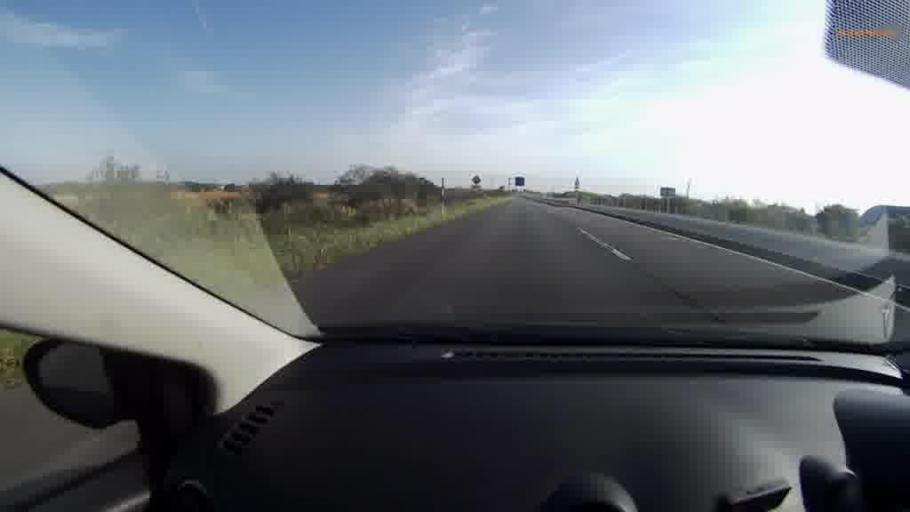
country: JP
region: Hokkaido
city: Kushiro
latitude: 43.0325
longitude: 144.3074
